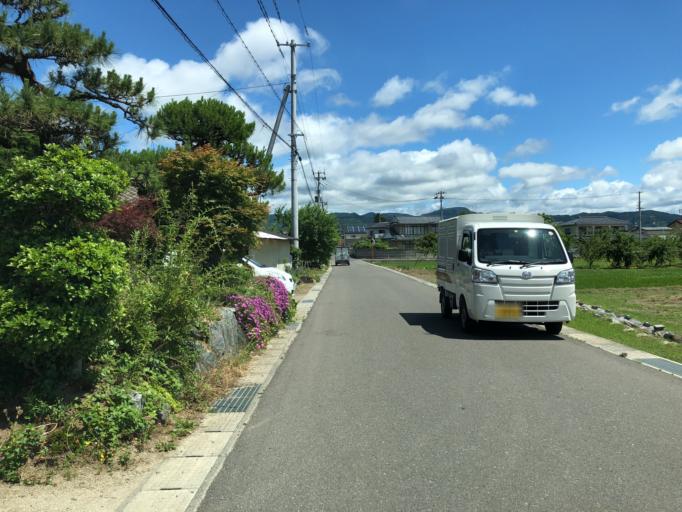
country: JP
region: Fukushima
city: Fukushima-shi
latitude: 37.8034
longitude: 140.4360
